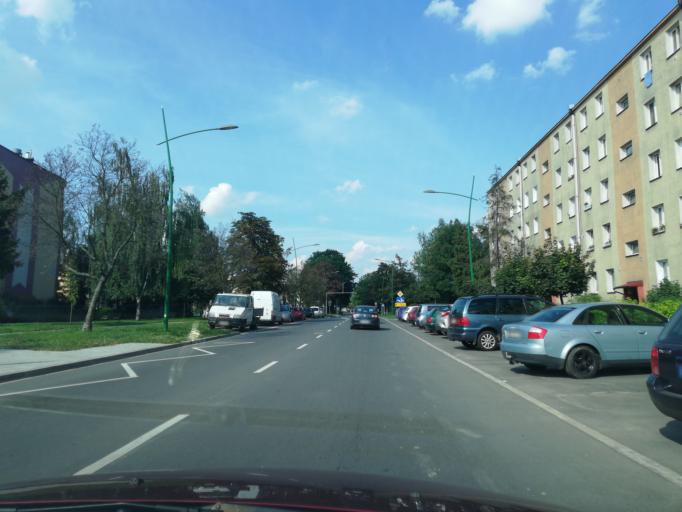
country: PL
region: Lesser Poland Voivodeship
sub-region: Powiat nowosadecki
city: Nowy Sacz
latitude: 49.6256
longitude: 20.7061
